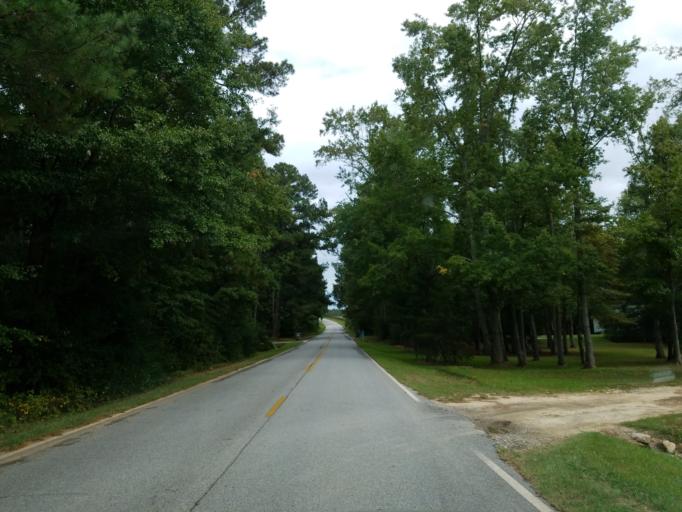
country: US
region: Georgia
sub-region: Lamar County
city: Barnesville
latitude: 33.0101
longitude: -84.1048
